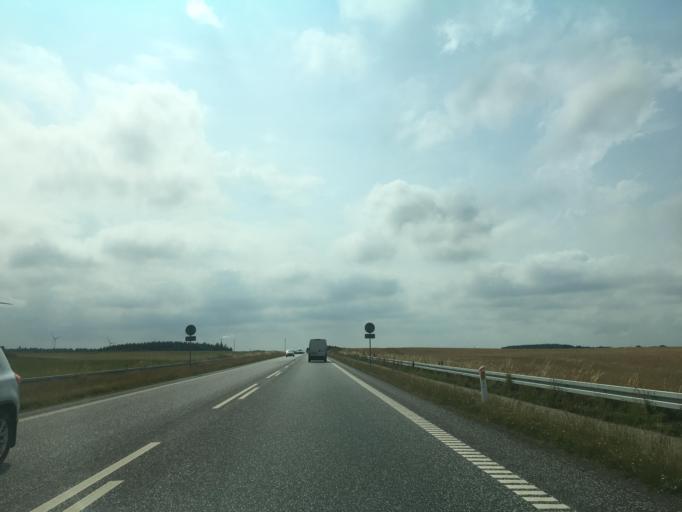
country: DK
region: Central Jutland
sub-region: Struer Kommune
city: Struer
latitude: 56.4264
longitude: 8.5993
